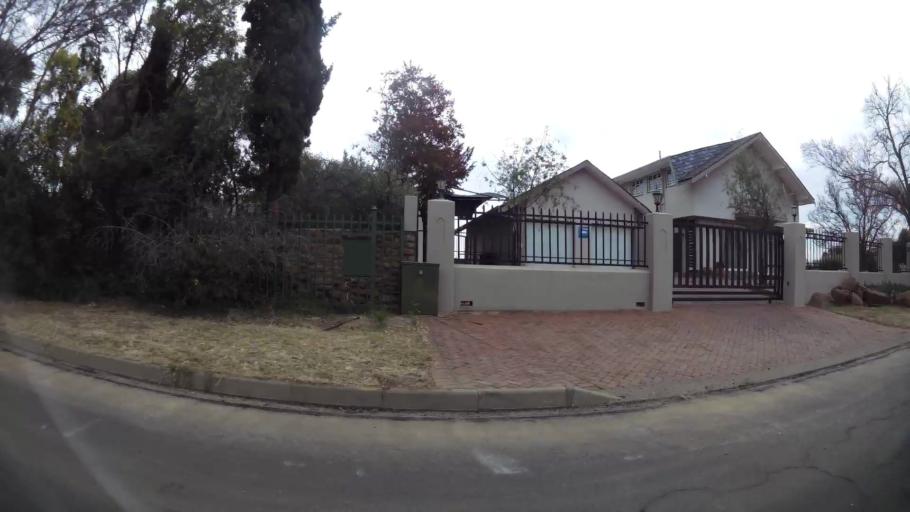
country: ZA
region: Orange Free State
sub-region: Mangaung Metropolitan Municipality
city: Bloemfontein
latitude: -29.0975
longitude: 26.2112
